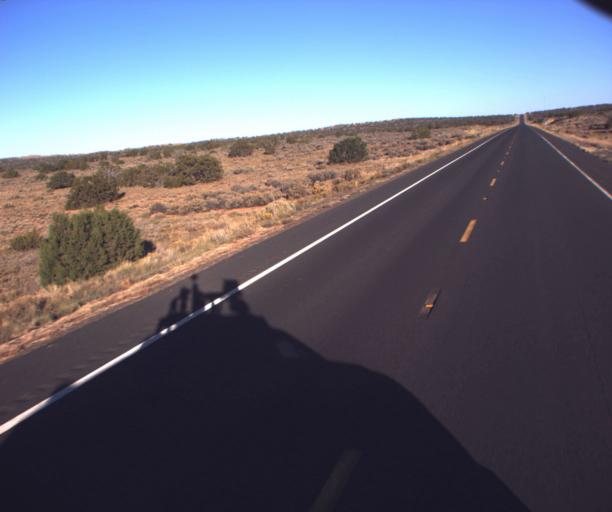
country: US
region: Arizona
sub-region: Apache County
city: Houck
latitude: 35.3295
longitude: -109.4384
